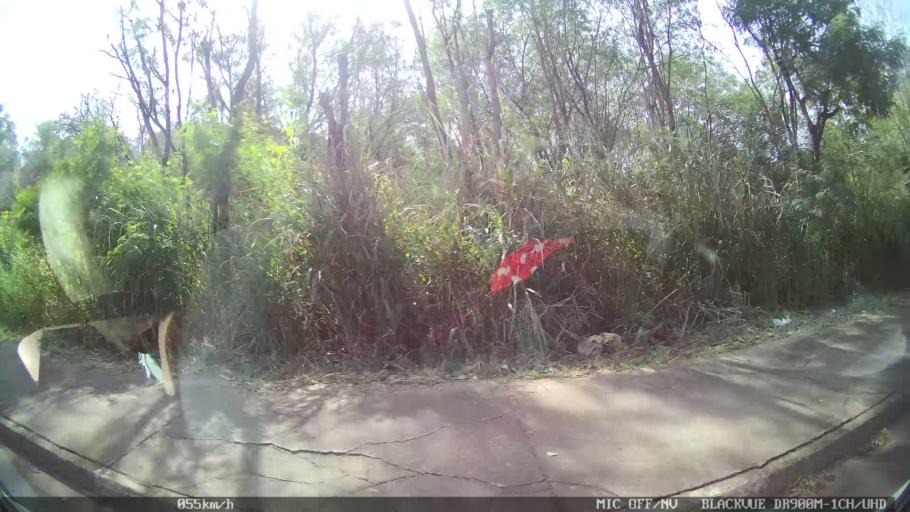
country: BR
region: Sao Paulo
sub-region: Piracicaba
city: Piracicaba
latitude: -22.7586
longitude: -47.6034
